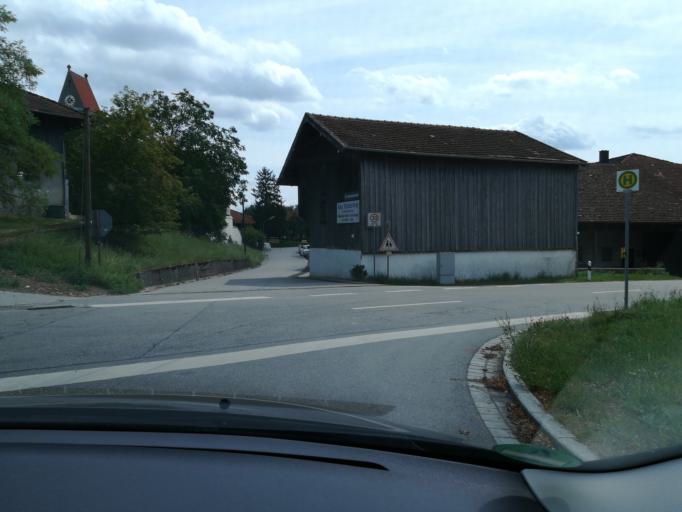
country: DE
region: Bavaria
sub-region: Upper Bavaria
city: Assling
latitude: 47.9923
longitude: 11.9715
